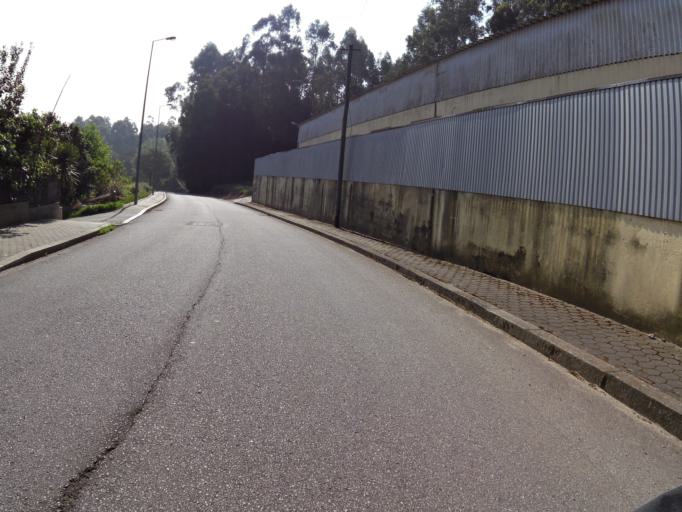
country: PT
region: Aveiro
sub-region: Santa Maria da Feira
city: Argoncilhe
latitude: 41.0339
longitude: -8.5480
